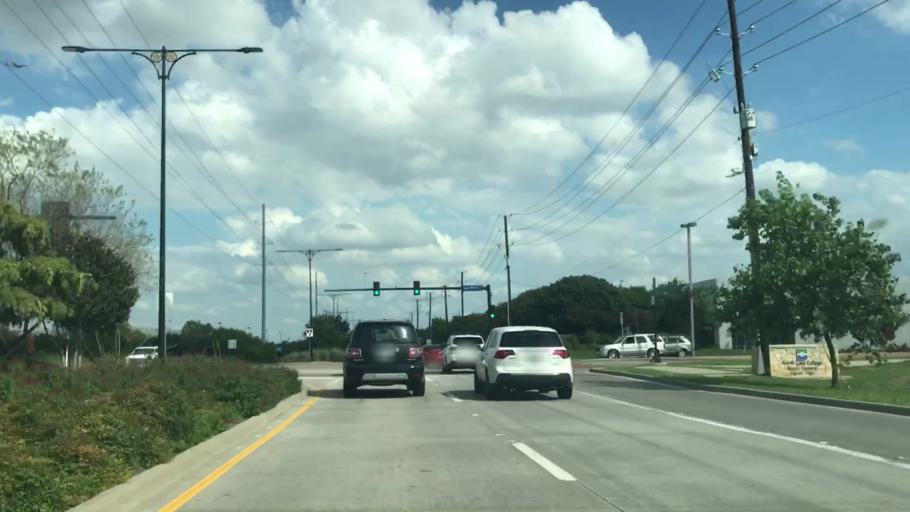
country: US
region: Texas
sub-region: Dallas County
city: Coppell
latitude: 32.9730
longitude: -97.0255
